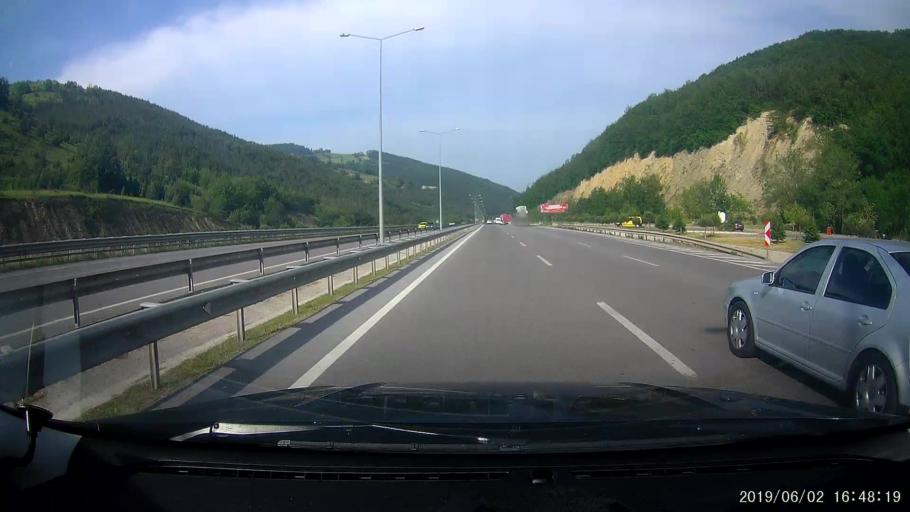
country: TR
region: Samsun
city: Kavak
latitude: 41.2258
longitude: 36.1330
